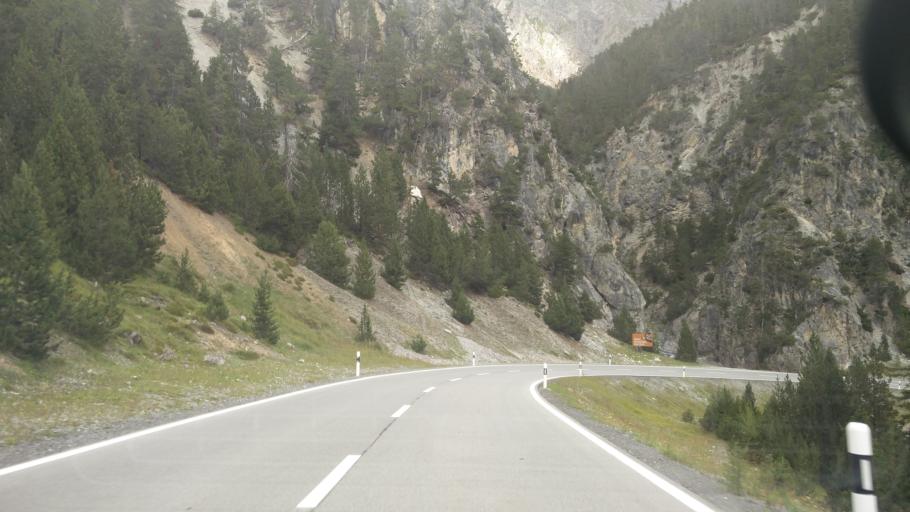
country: CH
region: Grisons
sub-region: Inn District
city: Zernez
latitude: 46.6800
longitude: 10.1647
